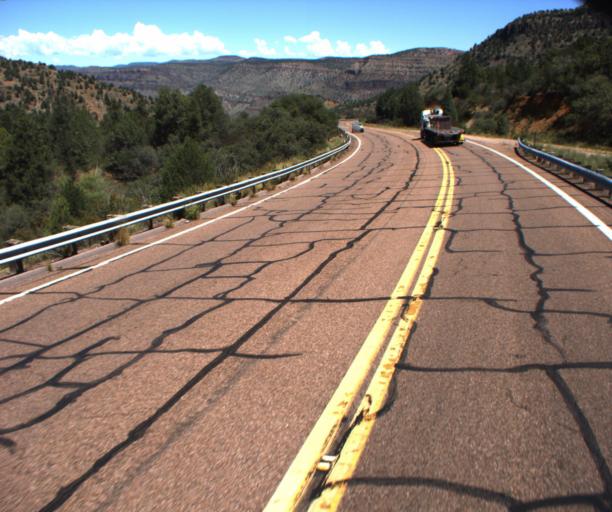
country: US
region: Arizona
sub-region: Navajo County
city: Cibecue
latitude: 33.7754
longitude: -110.5050
